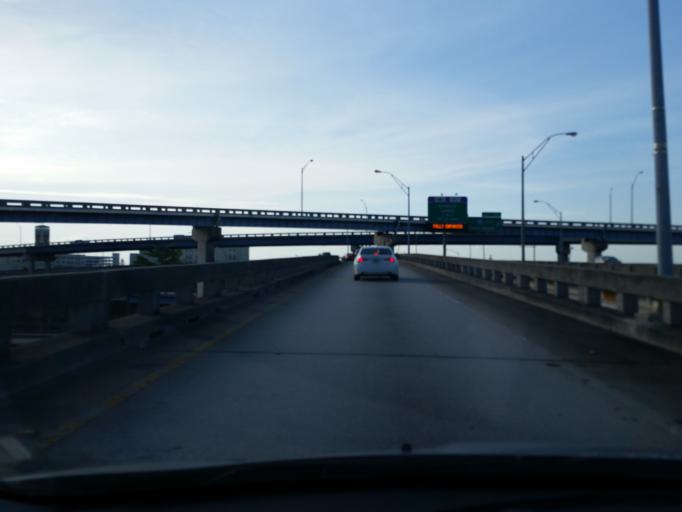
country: US
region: Florida
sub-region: Miami-Dade County
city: Miami
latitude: 25.7877
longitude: -80.2033
